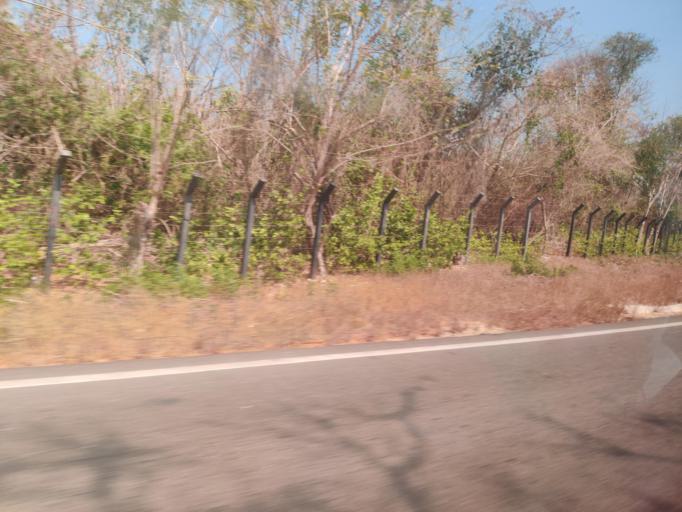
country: CO
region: Bolivar
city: Turbana
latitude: 10.1745
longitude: -75.6464
